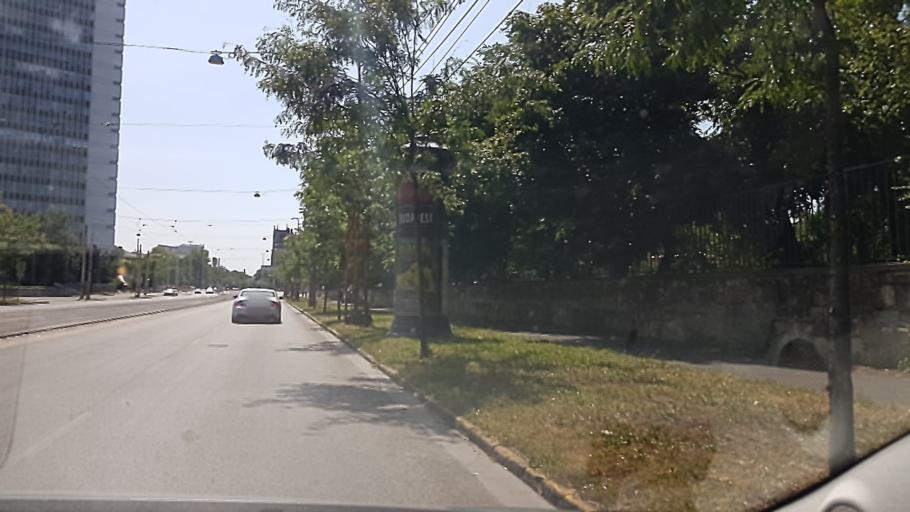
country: HU
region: Budapest
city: Budapest VIII. keruelet
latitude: 47.4806
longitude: 19.0930
